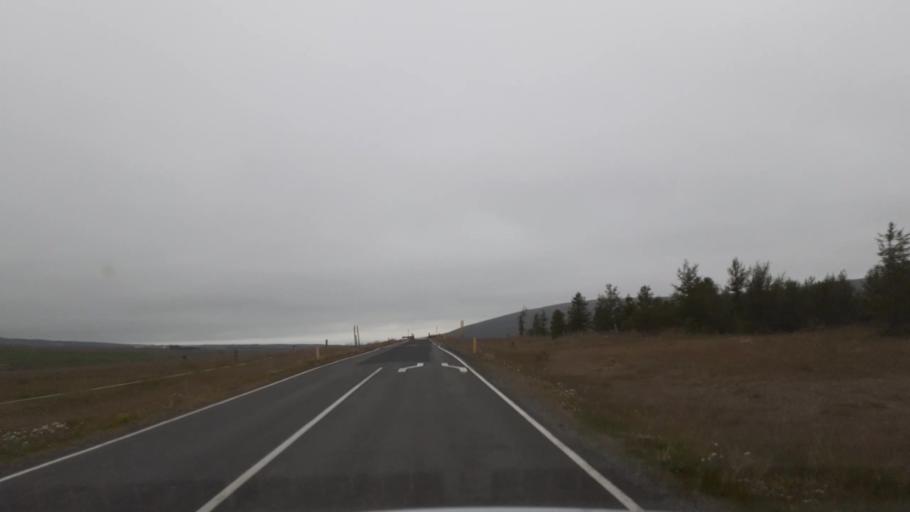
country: IS
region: Northeast
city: Siglufjoerdur
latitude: 65.7388
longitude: -19.1347
